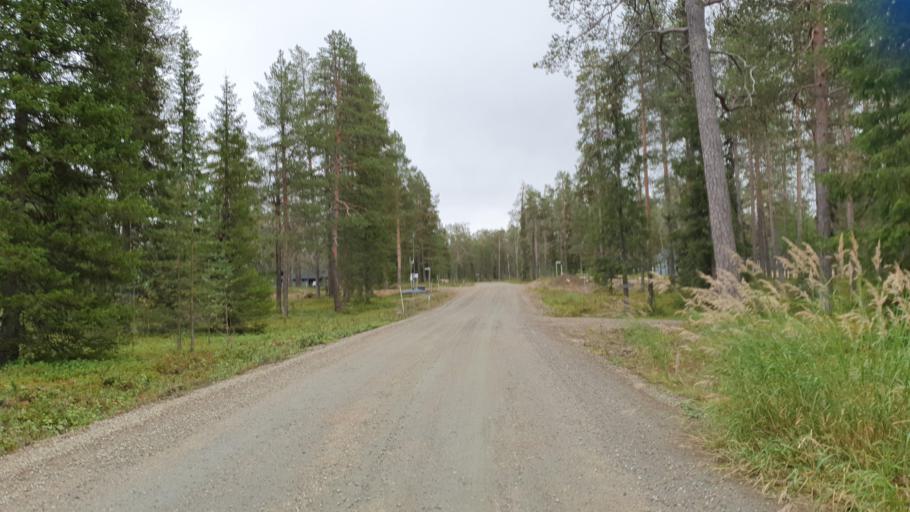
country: FI
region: Lapland
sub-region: Tunturi-Lappi
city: Kolari
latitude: 67.5985
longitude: 24.1849
